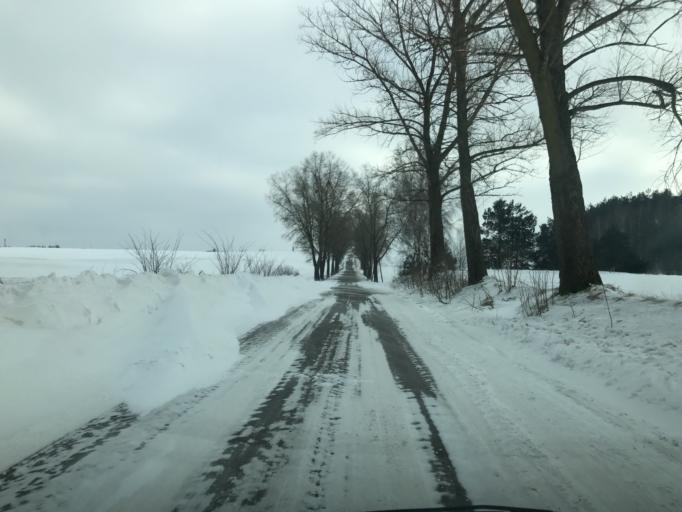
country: PL
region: Warmian-Masurian Voivodeship
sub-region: Powiat dzialdowski
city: Rybno
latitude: 53.4232
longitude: 19.8612
